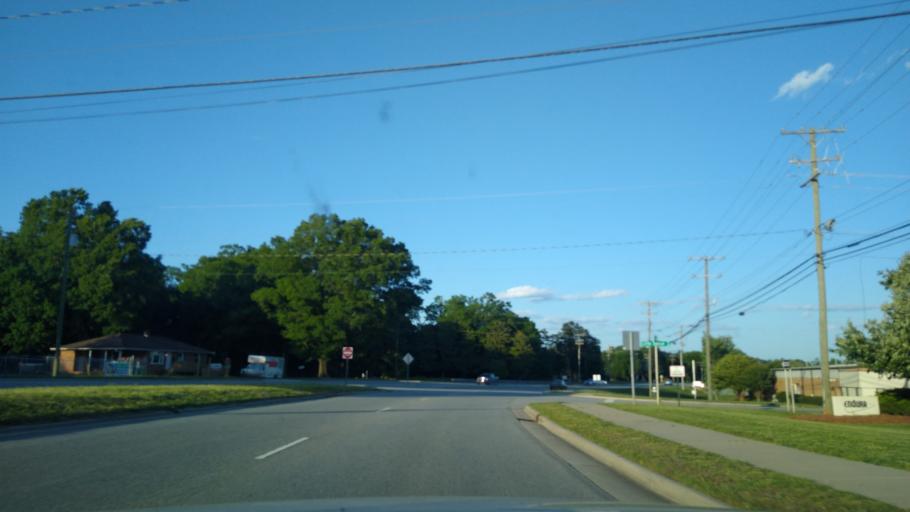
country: US
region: North Carolina
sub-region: Guilford County
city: Oak Ridge
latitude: 36.1042
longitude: -79.9891
